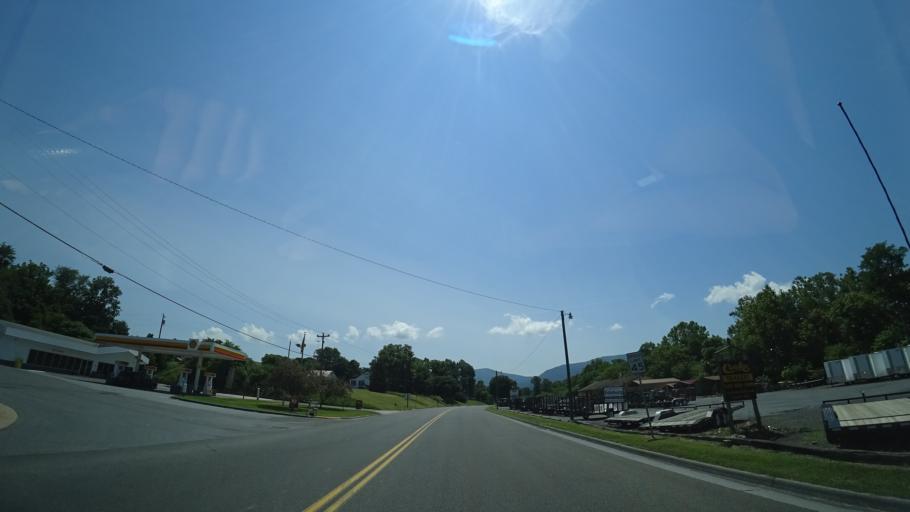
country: US
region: Virginia
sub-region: Shenandoah County
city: Edinburg
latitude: 38.8293
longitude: -78.5746
